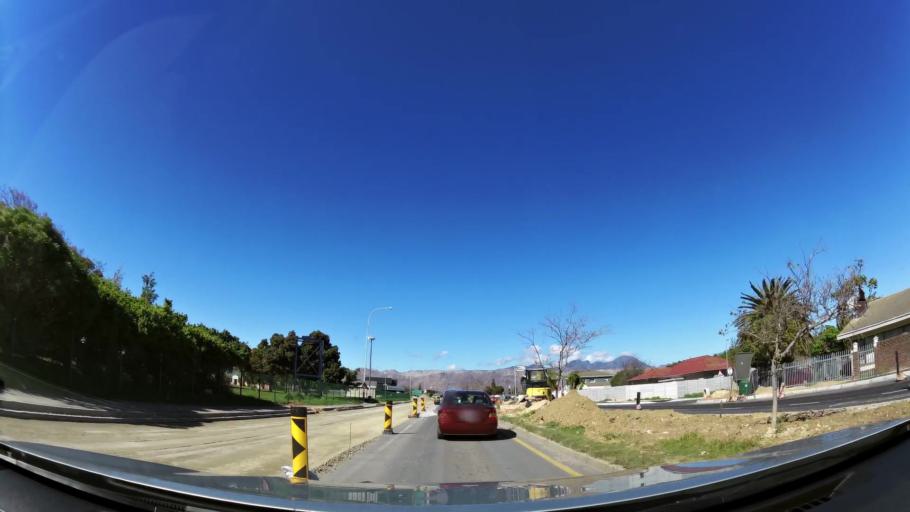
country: ZA
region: Western Cape
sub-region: Cape Winelands District Municipality
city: Stellenbosch
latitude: -34.1060
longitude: 18.8366
